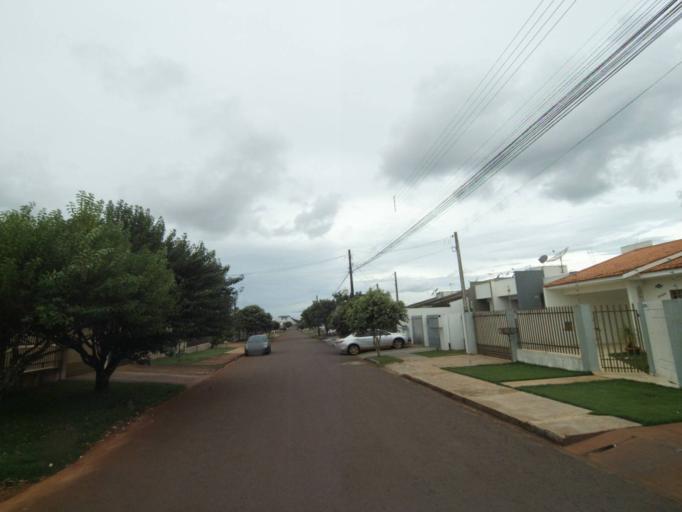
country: BR
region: Parana
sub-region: Campo Mourao
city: Campo Mourao
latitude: -24.0267
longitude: -52.3588
